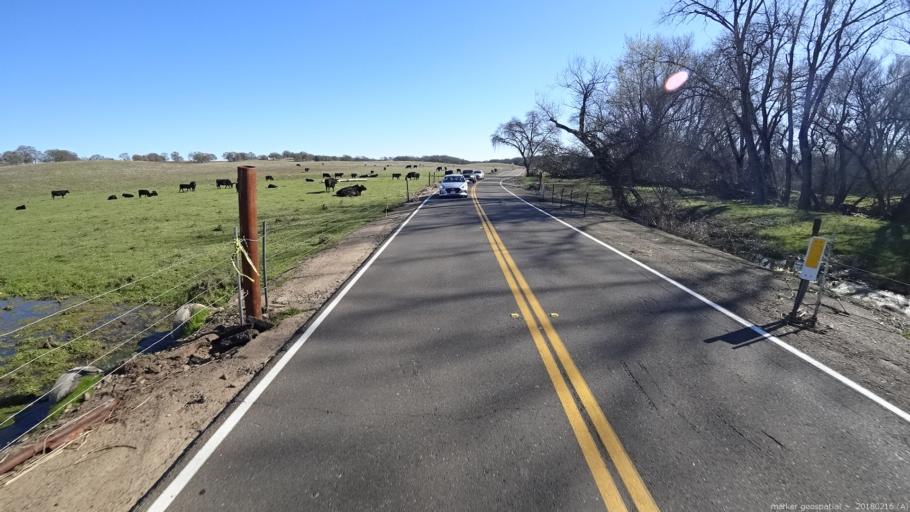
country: US
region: California
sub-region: Sacramento County
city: Rancho Murieta
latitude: 38.5493
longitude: -121.1130
